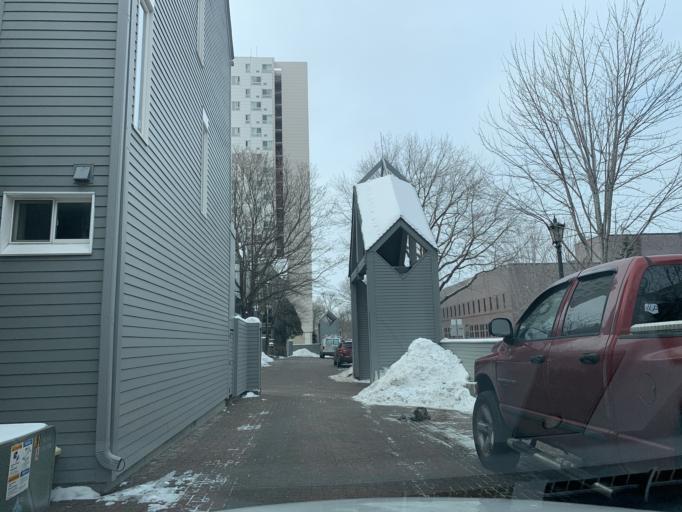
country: US
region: Minnesota
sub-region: Hennepin County
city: Minneapolis
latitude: 44.9719
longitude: -93.2811
